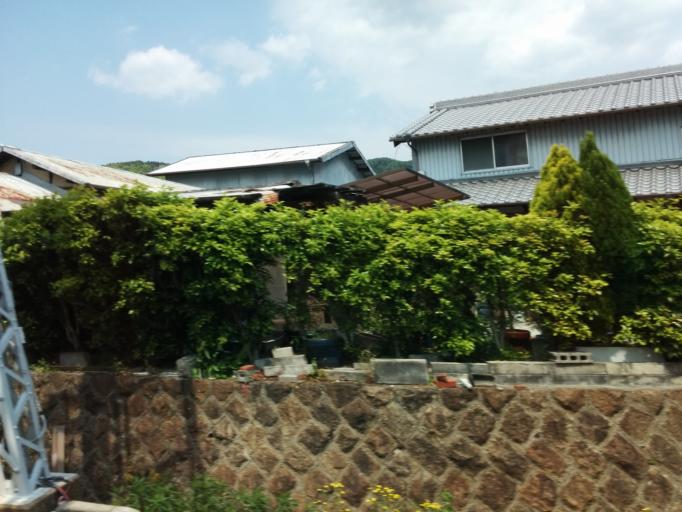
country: JP
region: Osaka
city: Takatsuki
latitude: 34.8630
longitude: 135.6506
